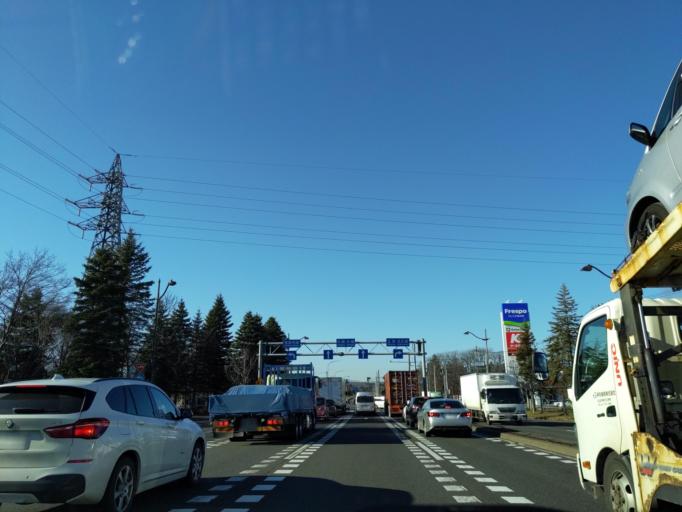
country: JP
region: Hokkaido
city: Kitahiroshima
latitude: 42.9017
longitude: 141.5715
